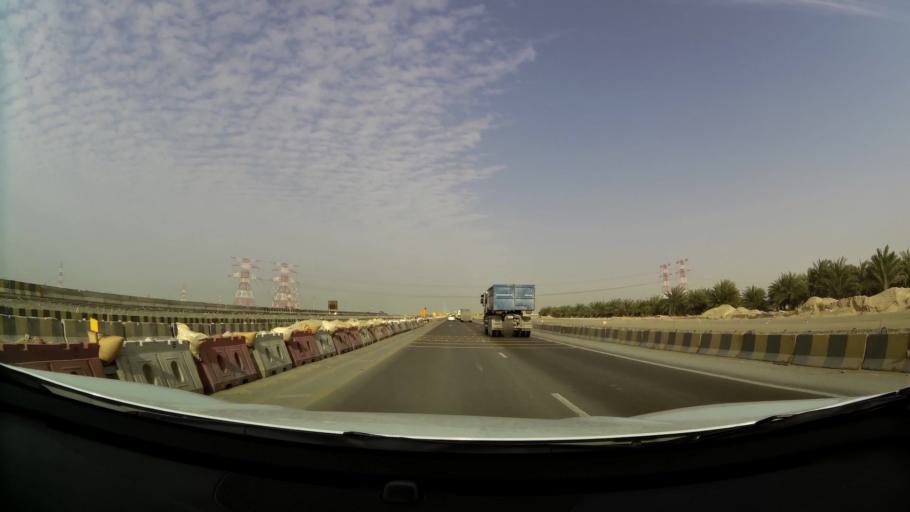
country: AE
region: Abu Dhabi
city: Abu Dhabi
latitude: 24.2181
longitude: 54.4262
